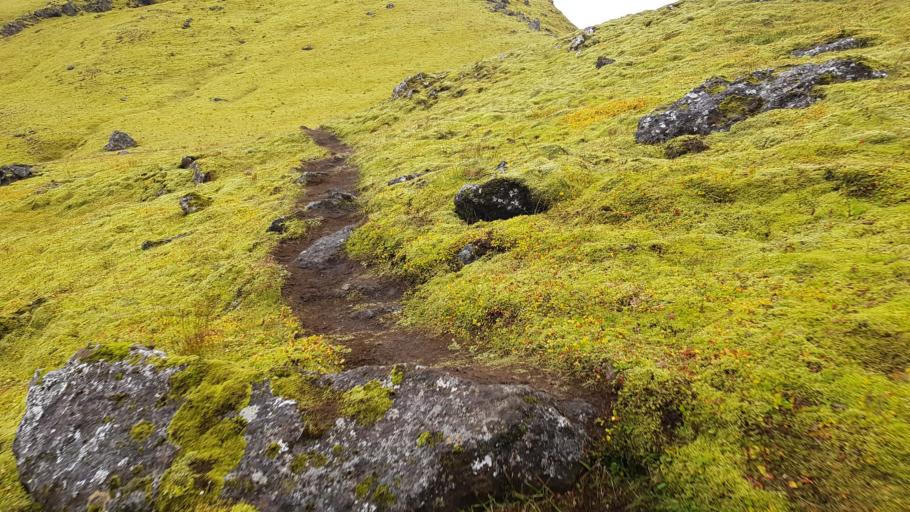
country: IS
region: South
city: Vestmannaeyjar
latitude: 63.5375
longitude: -18.8546
